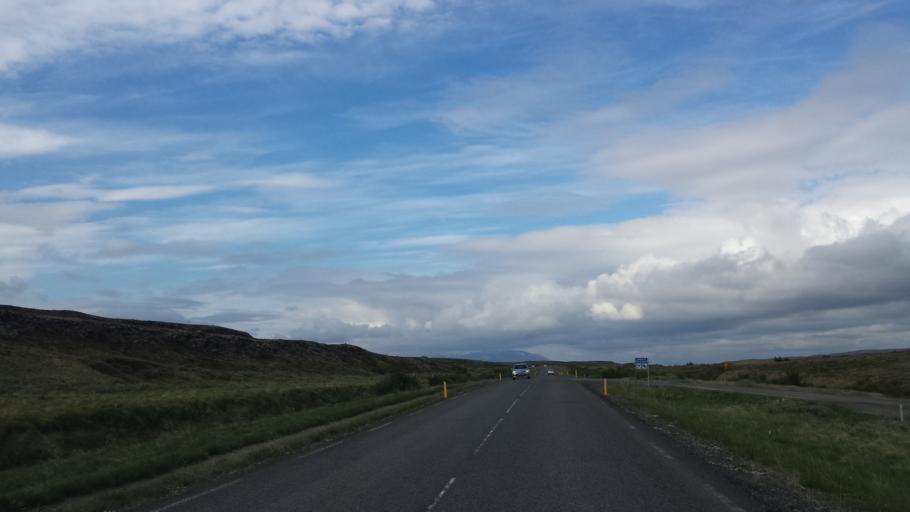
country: IS
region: South
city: Vestmannaeyjar
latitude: 64.3074
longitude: -20.1637
